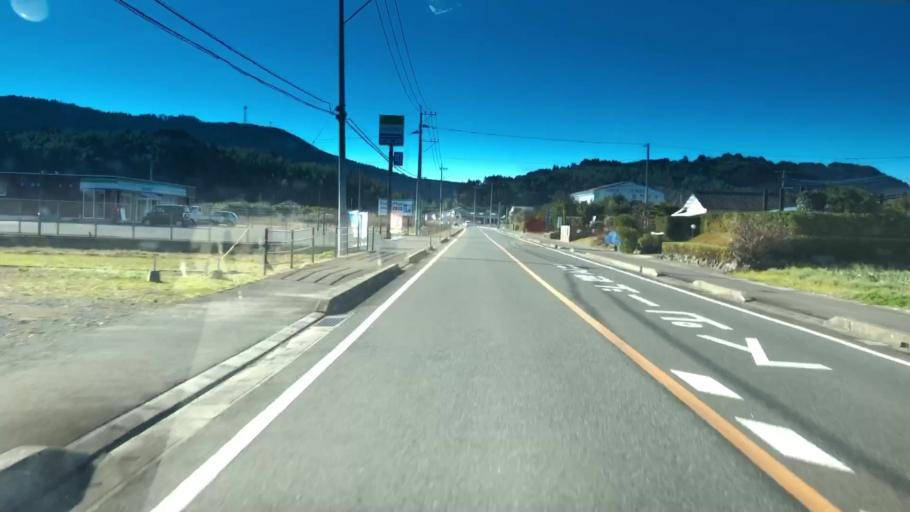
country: JP
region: Kagoshima
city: Satsumasendai
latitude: 31.8173
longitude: 130.2808
